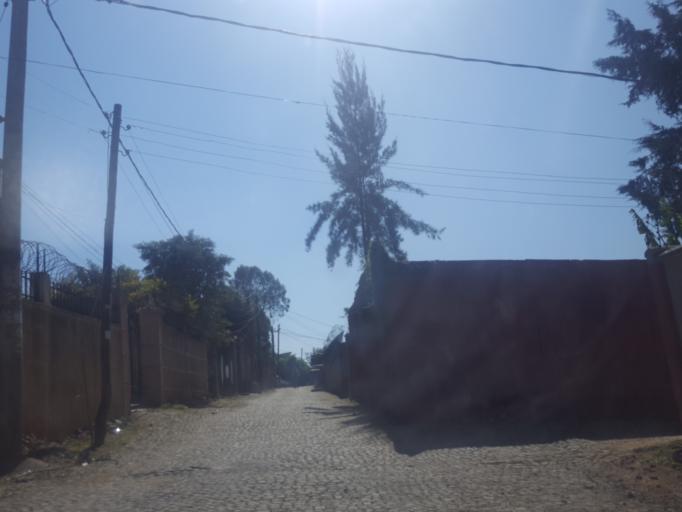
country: ET
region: Adis Abeba
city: Addis Ababa
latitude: 9.0549
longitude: 38.7242
